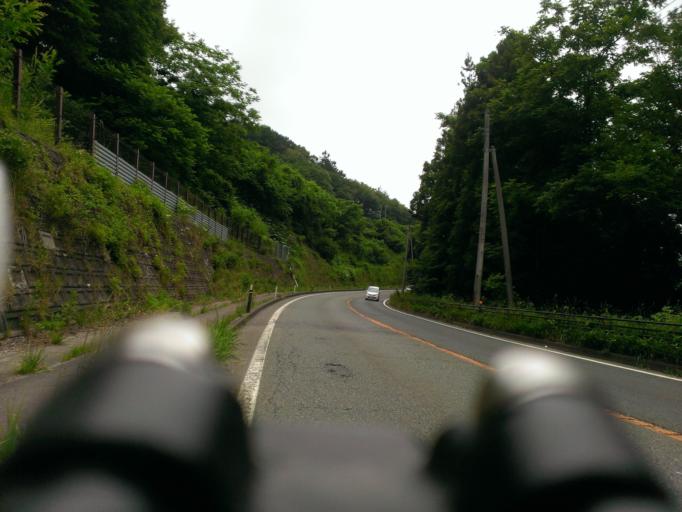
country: JP
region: Iwate
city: Morioka-shi
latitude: 39.8290
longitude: 141.1490
